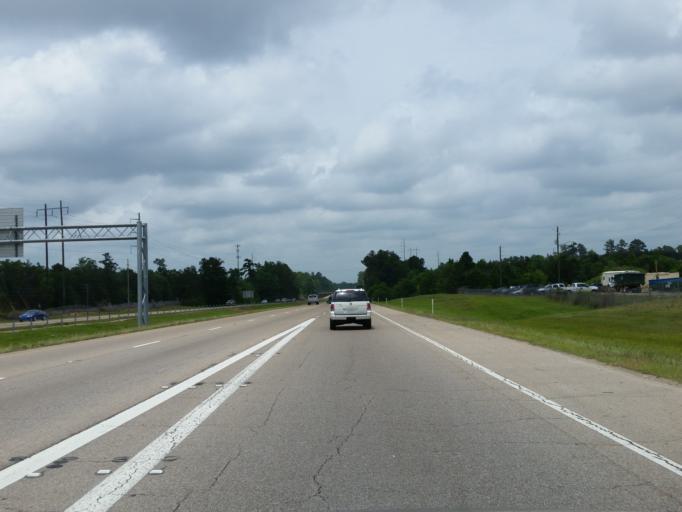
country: US
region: Mississippi
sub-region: Lamar County
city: Arnold Line
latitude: 31.3306
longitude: -89.3521
